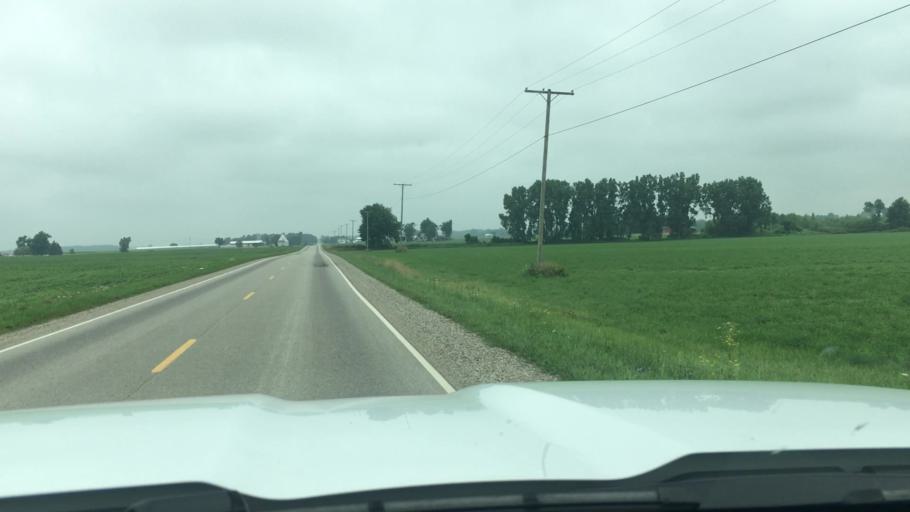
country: US
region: Michigan
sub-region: Sanilac County
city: Brown City
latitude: 43.2786
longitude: -82.9827
